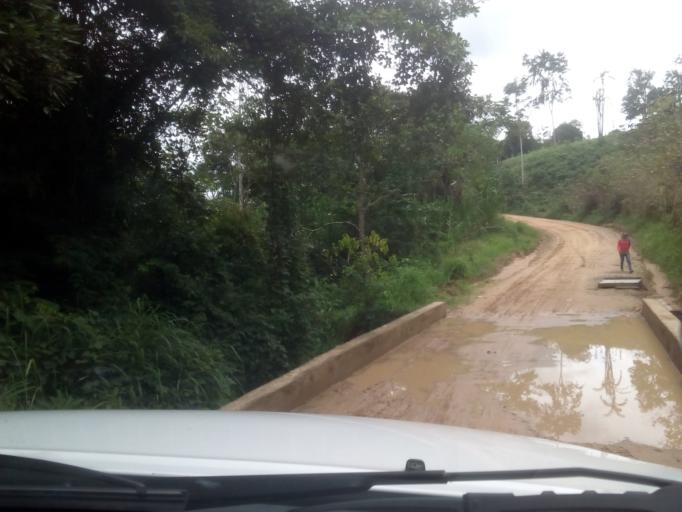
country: PE
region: San Martin
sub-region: Provincia de Lamas
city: Lamas
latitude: -6.4274
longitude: -76.4561
